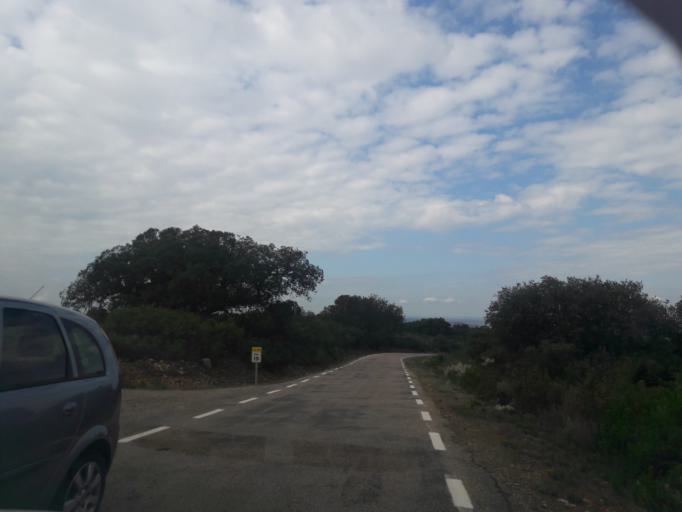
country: ES
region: Castille and Leon
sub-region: Provincia de Salamanca
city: Serradilla del Arroyo
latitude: 40.5406
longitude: -6.3907
